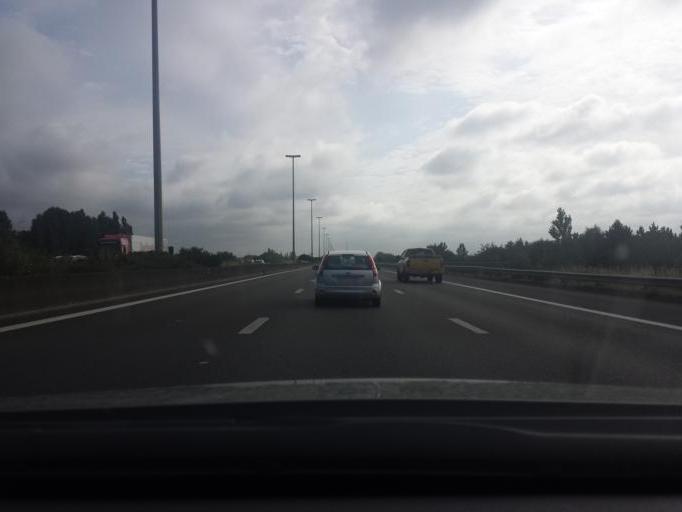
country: BE
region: Flanders
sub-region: Provincie West-Vlaanderen
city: Zwevegem
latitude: 50.8323
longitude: 3.3303
